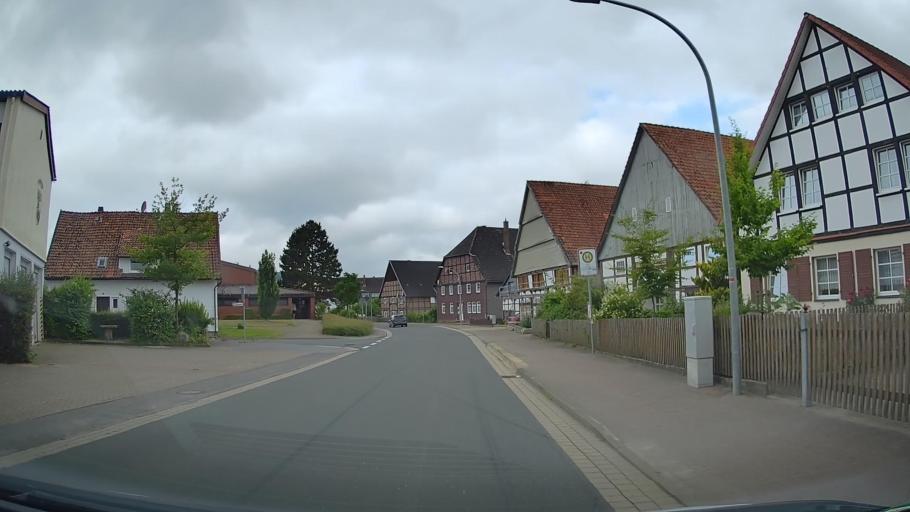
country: DE
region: Lower Saxony
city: Aerzen
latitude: 52.0300
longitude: 9.2329
